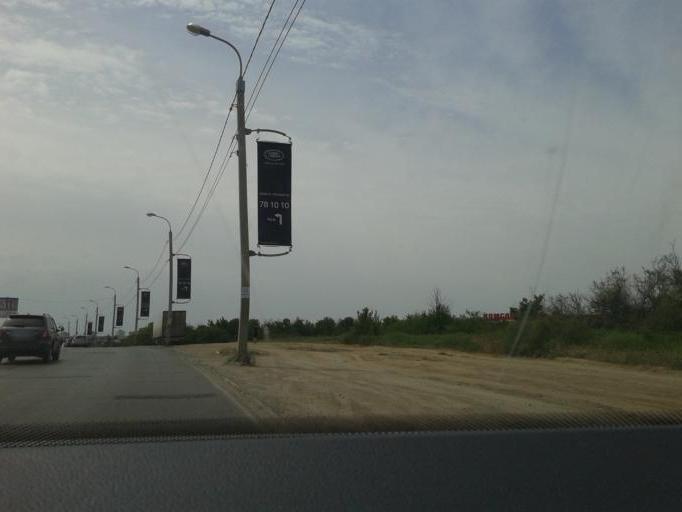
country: RU
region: Volgograd
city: Volgograd
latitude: 48.7473
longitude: 44.5250
